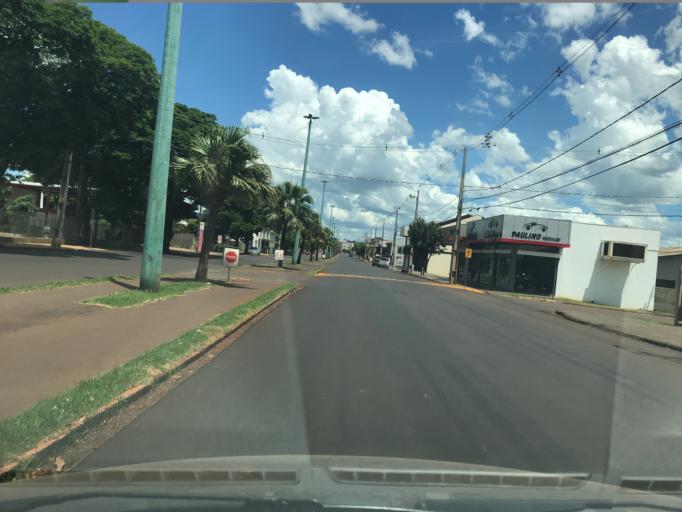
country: BR
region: Parana
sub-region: Palotina
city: Palotina
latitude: -24.2740
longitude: -53.8417
